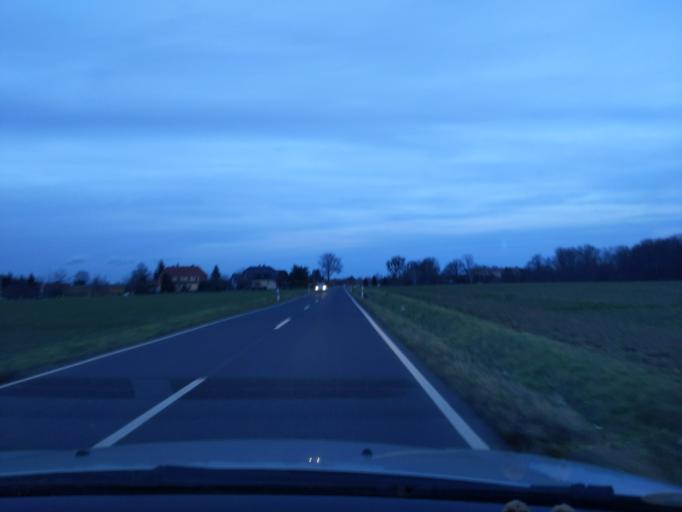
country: DE
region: Saxony
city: Guttau
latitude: 51.2550
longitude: 14.5514
